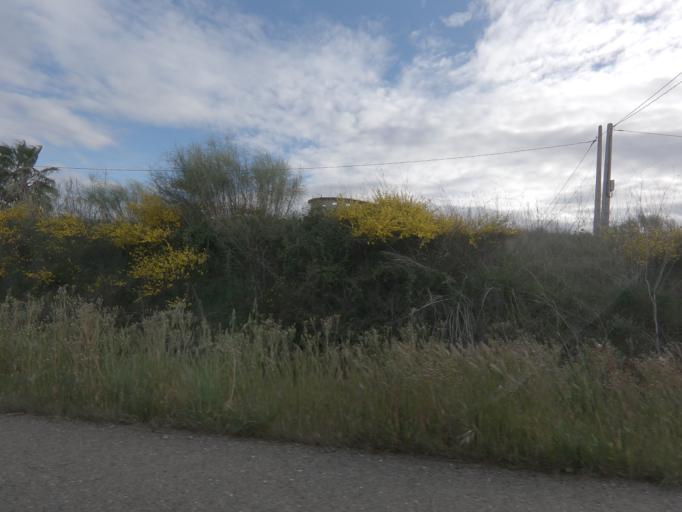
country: ES
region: Extremadura
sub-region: Provincia de Caceres
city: Coria
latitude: 39.9969
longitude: -6.5457
